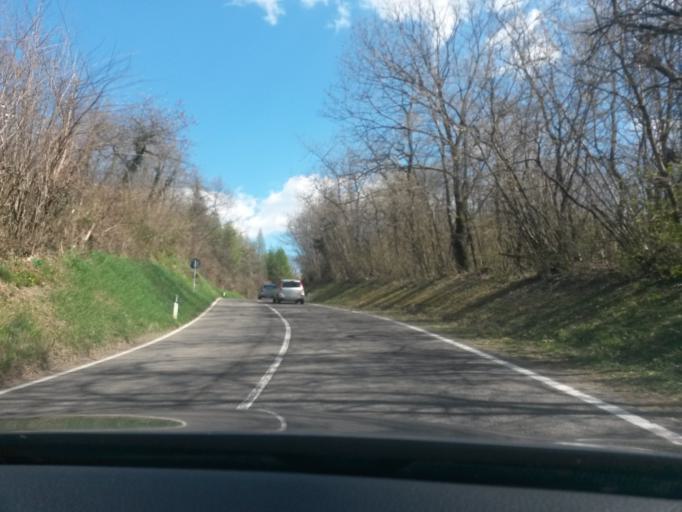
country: IT
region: Trentino-Alto Adige
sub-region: Bolzano
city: San Michele
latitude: 46.4416
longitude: 11.2790
